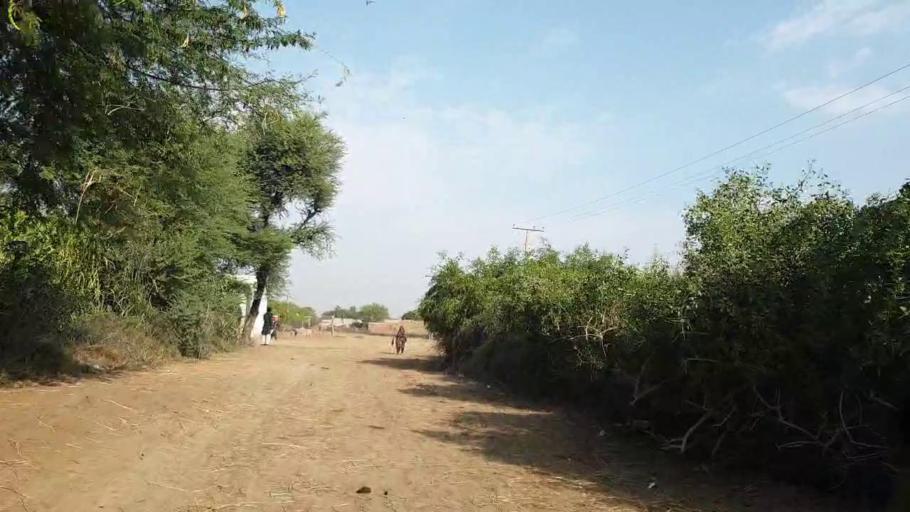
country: PK
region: Sindh
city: Tando Muhammad Khan
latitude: 25.0401
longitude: 68.4172
